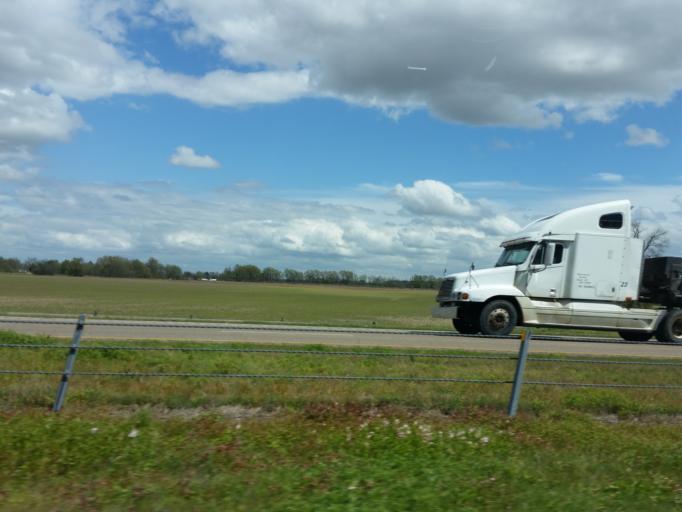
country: US
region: Arkansas
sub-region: Crittenden County
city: Marion
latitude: 35.2704
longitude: -90.2322
